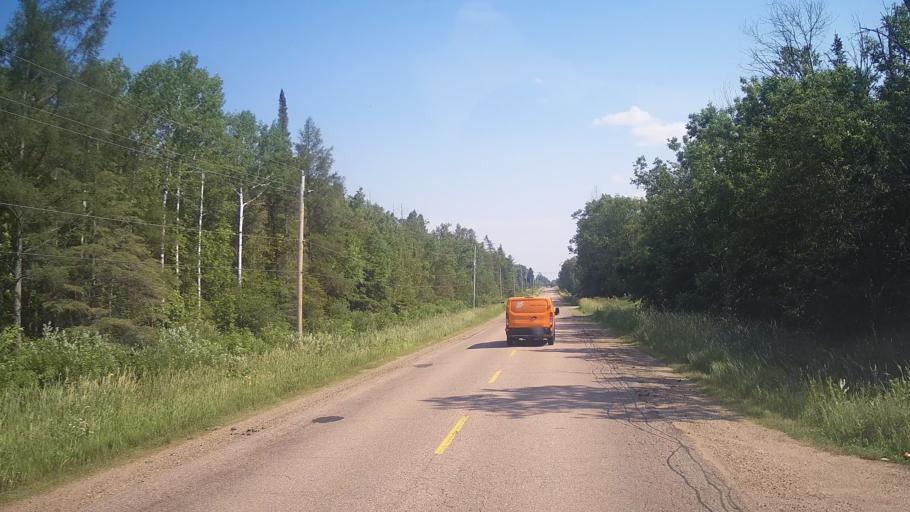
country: CA
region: Ontario
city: Pembroke
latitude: 45.5979
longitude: -77.2318
